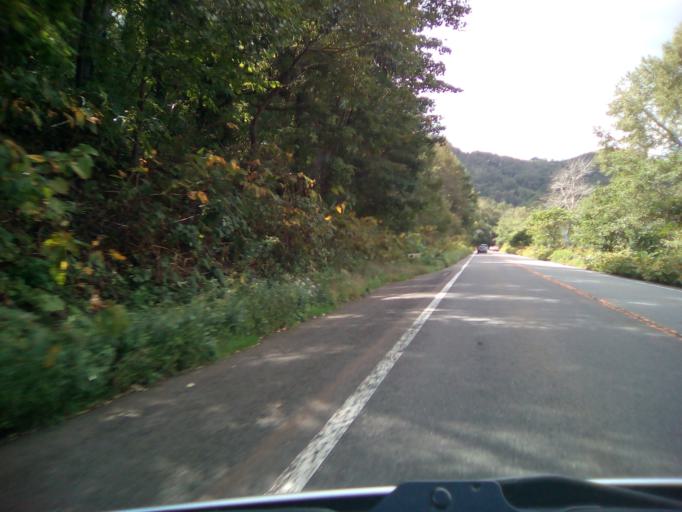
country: JP
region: Hokkaido
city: Date
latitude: 42.5905
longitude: 140.7871
